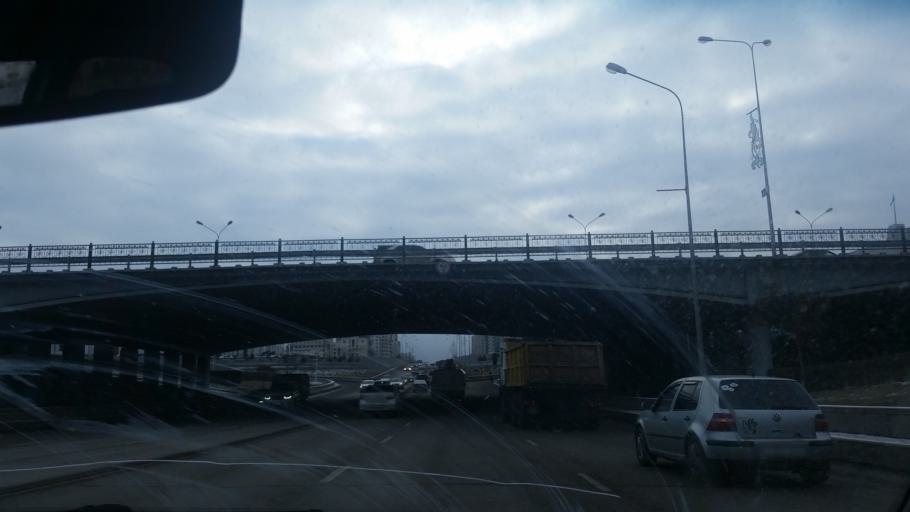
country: KZ
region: Astana Qalasy
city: Astana
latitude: 51.1226
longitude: 71.4366
